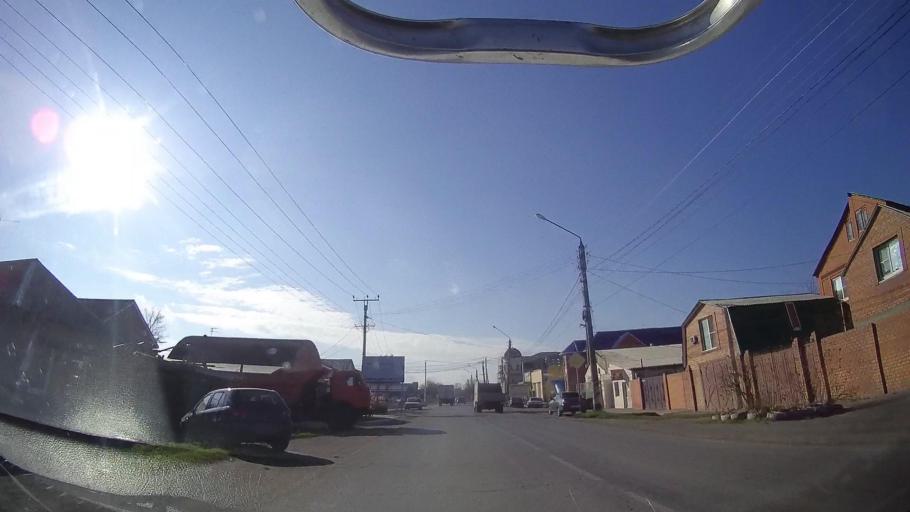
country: RU
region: Rostov
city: Bataysk
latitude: 47.1276
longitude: 39.6938
